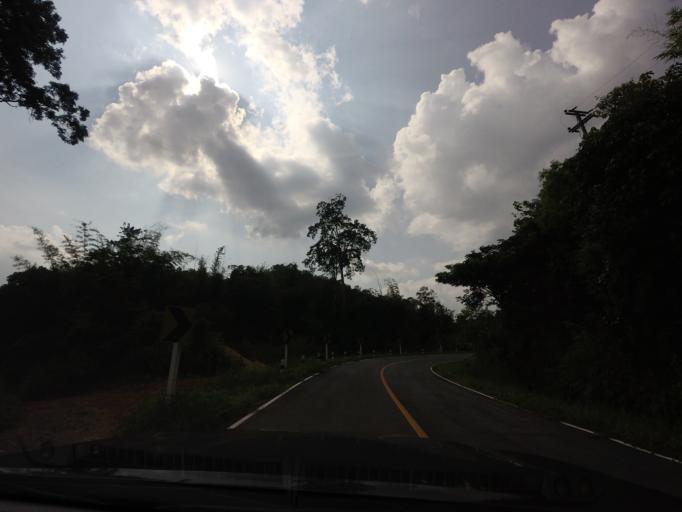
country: TH
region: Uttaradit
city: Ban Khok
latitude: 18.1911
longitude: 101.0522
